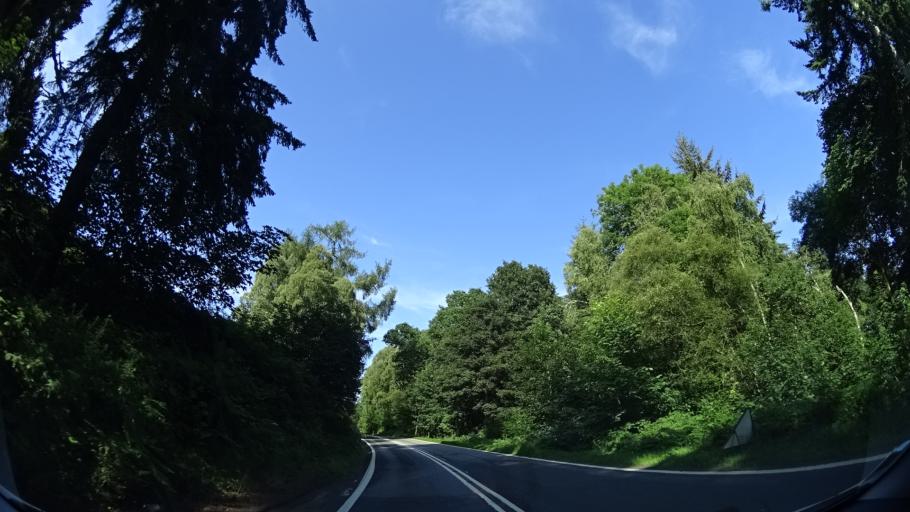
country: GB
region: Scotland
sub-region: Highland
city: Inverness
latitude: 57.4389
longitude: -4.2992
